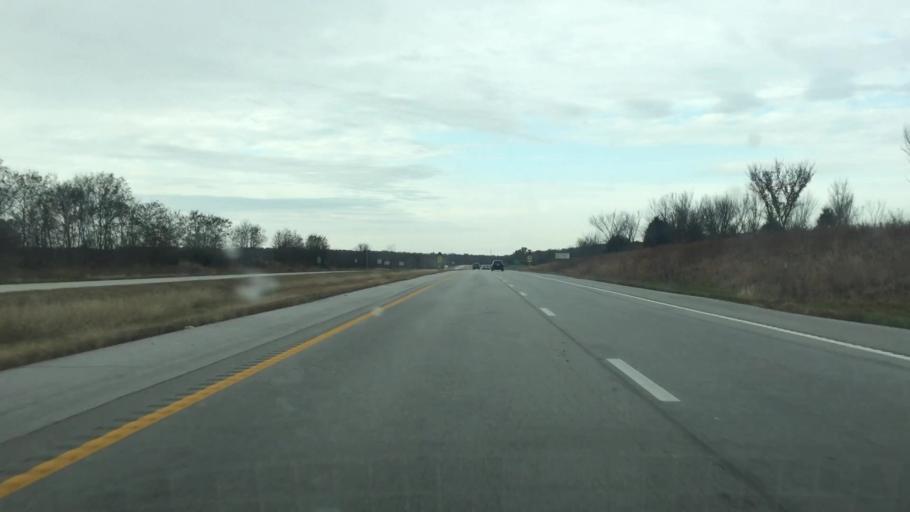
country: US
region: Missouri
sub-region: Saint Clair County
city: Osceola
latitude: 38.2030
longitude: -93.7503
